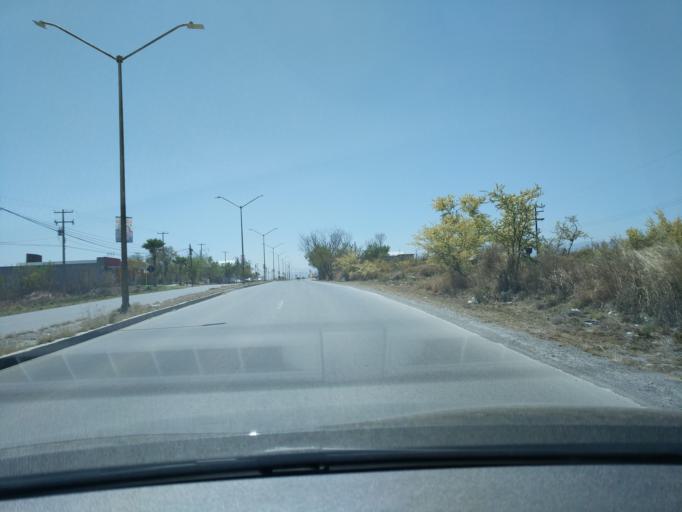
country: MX
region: Nuevo Leon
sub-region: Apodaca
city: Artemio Trevino
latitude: 25.8067
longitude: -100.1559
